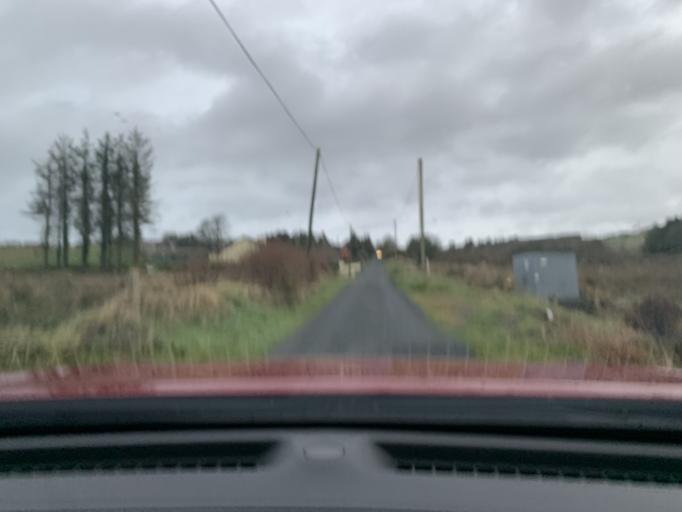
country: IE
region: Connaught
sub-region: Roscommon
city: Boyle
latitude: 53.9911
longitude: -8.3099
